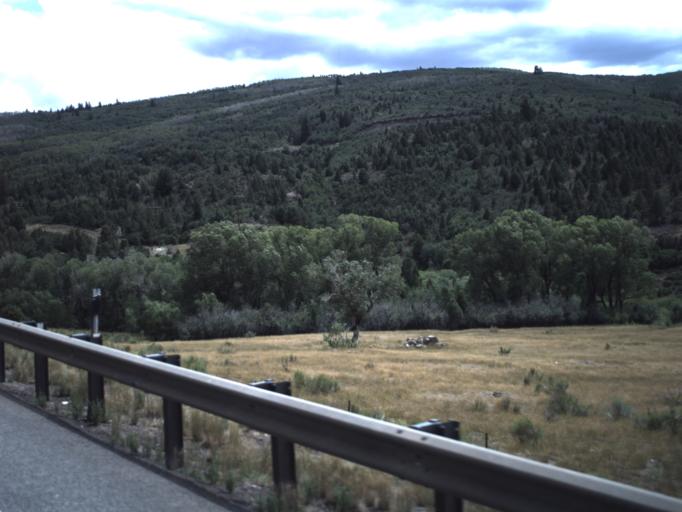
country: US
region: Utah
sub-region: Carbon County
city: Helper
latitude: 39.9357
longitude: -111.1325
